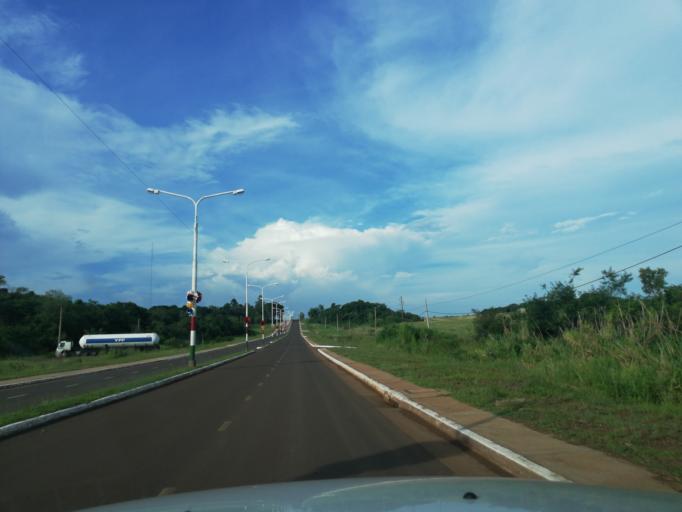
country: AR
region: Misiones
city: Garupa
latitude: -27.4690
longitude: -55.8263
